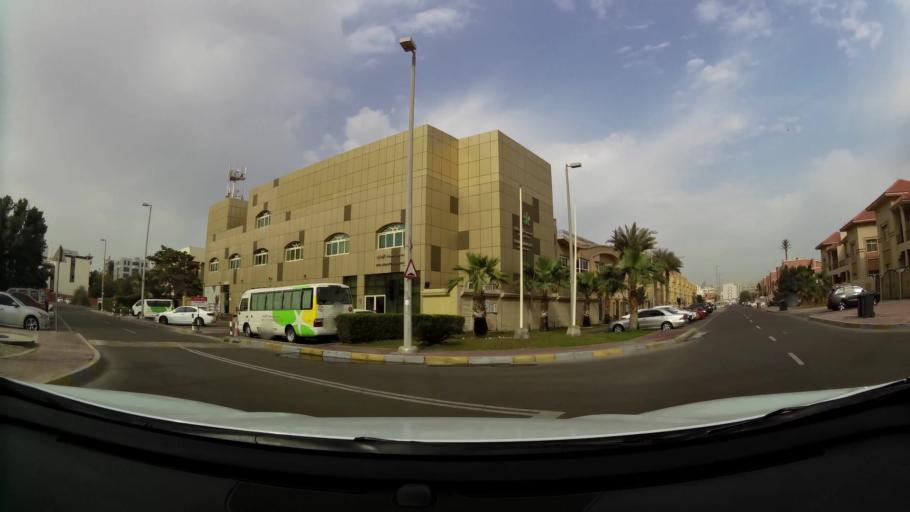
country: AE
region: Abu Dhabi
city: Abu Dhabi
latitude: 24.4708
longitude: 54.3833
